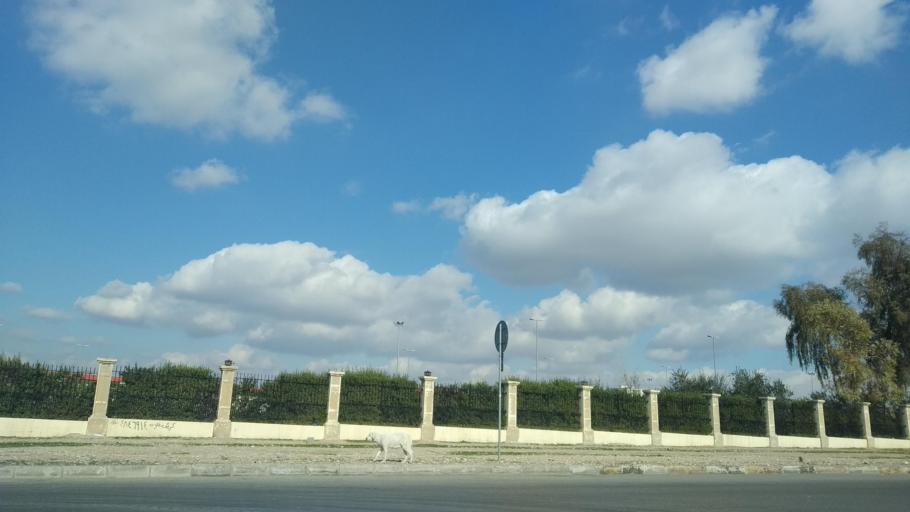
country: IQ
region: Arbil
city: Erbil
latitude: 36.2080
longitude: 44.1373
